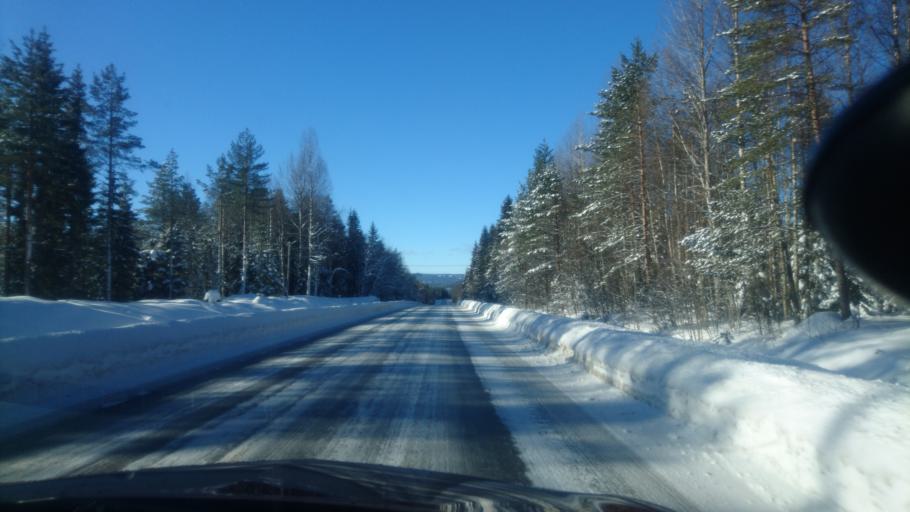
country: NO
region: Hedmark
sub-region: Trysil
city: Innbygda
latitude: 61.2650
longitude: 12.4265
